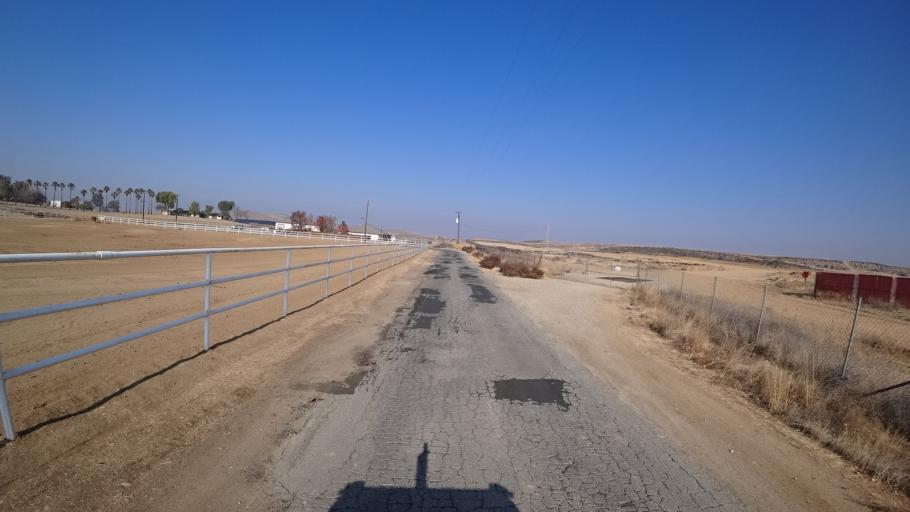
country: US
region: California
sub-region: Kern County
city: Oildale
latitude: 35.4137
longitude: -118.8788
